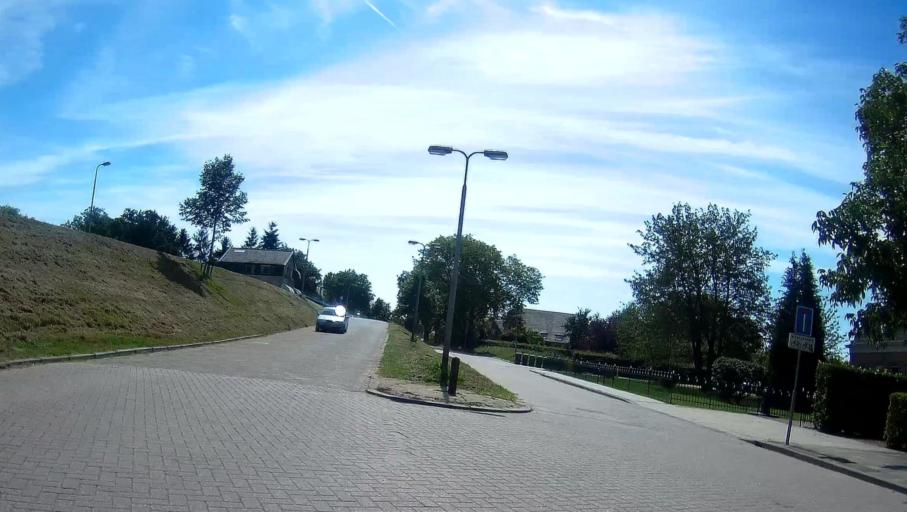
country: NL
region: South Holland
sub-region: Gemeente Ridderkerk
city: Ridderkerk
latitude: 51.8773
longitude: 4.6033
